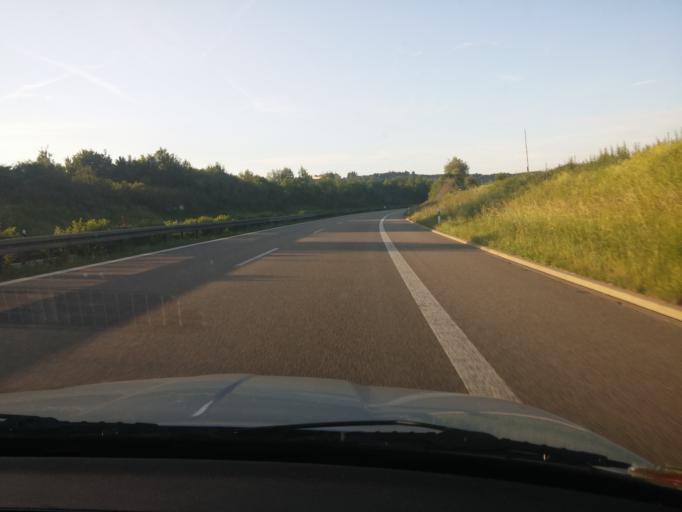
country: DE
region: Baden-Wuerttemberg
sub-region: Tuebingen Region
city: Leutkirch im Allgau
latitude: 47.8457
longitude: 9.9909
